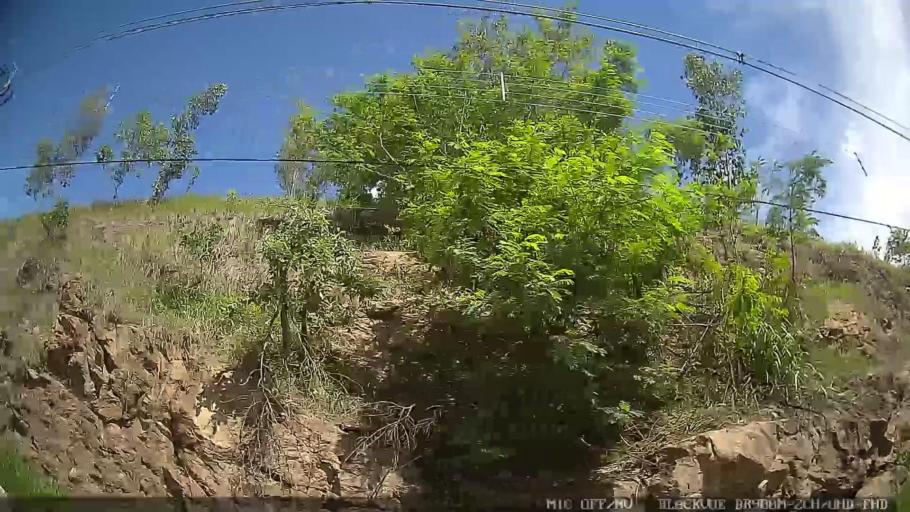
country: BR
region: Sao Paulo
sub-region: Pedreira
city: Pedreira
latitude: -22.7341
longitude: -46.8859
